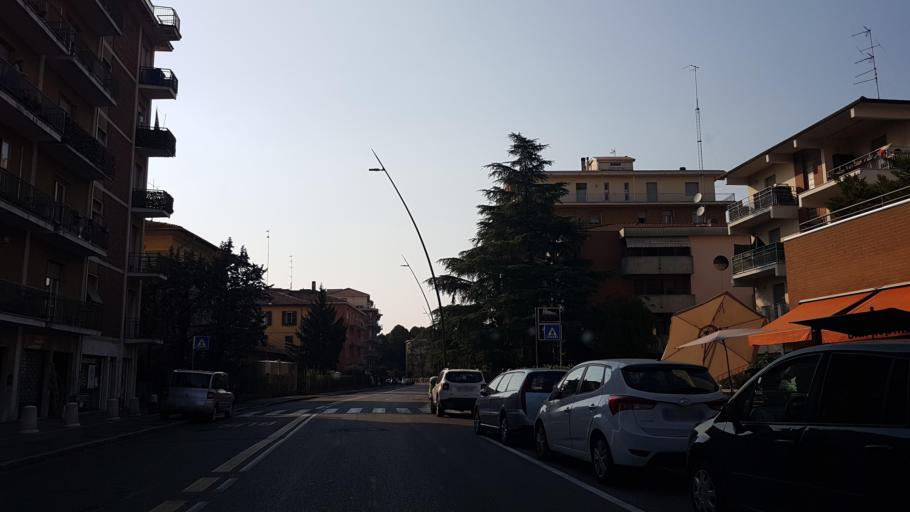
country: IT
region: Emilia-Romagna
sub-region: Provincia di Parma
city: Parma
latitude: 44.7961
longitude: 10.3162
